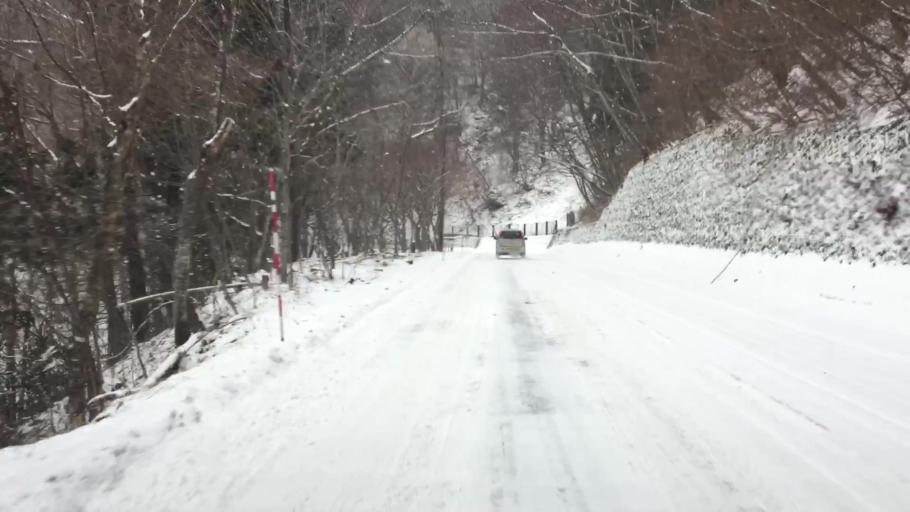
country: JP
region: Tochigi
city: Imaichi
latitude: 36.8856
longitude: 139.7320
